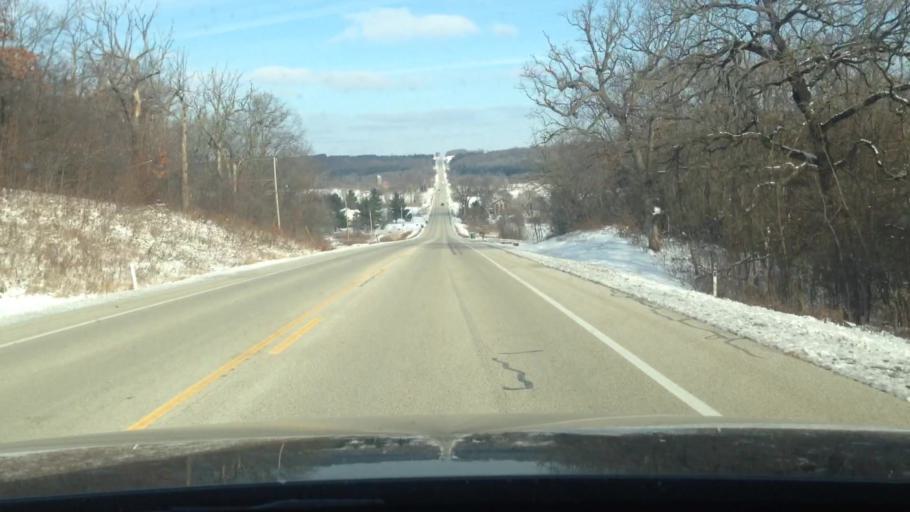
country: US
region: Wisconsin
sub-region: Walworth County
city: East Troy
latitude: 42.7186
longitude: -88.4055
